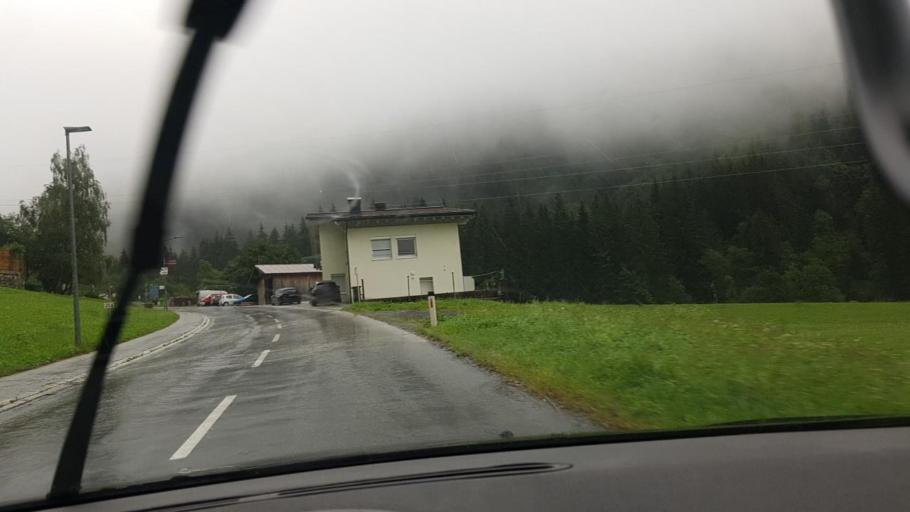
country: AT
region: Vorarlberg
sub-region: Politischer Bezirk Bludenz
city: Klosterle
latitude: 47.1313
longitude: 10.0983
